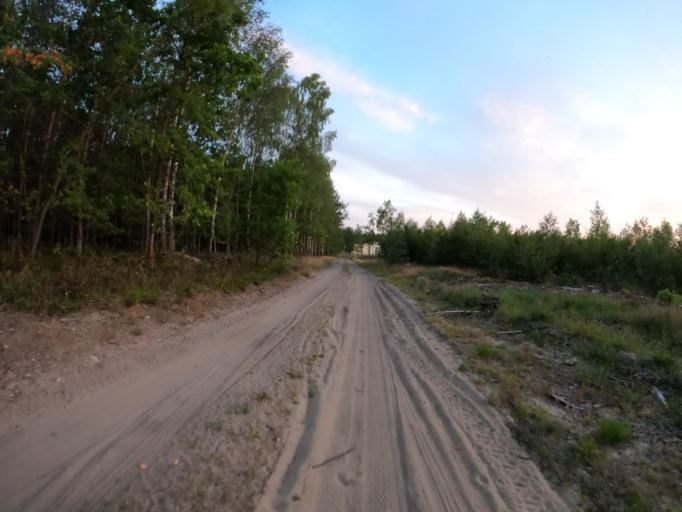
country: PL
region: West Pomeranian Voivodeship
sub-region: Powiat koszalinski
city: Sianow
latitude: 54.0809
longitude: 16.3990
